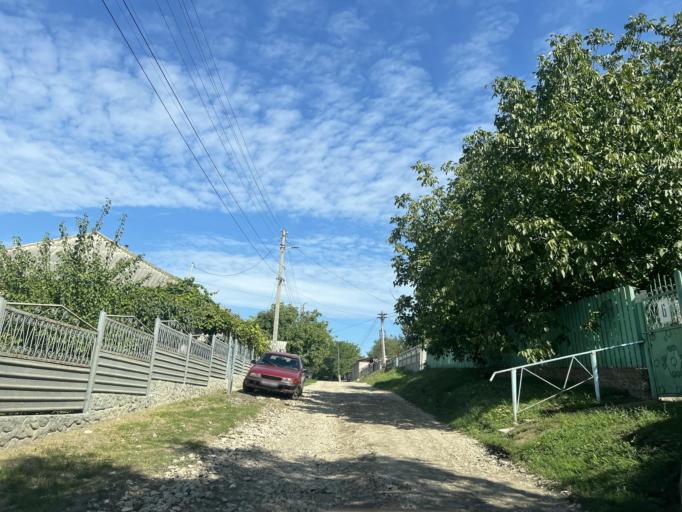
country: MD
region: Ungheni
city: Ungheni
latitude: 47.2024
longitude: 27.8111
